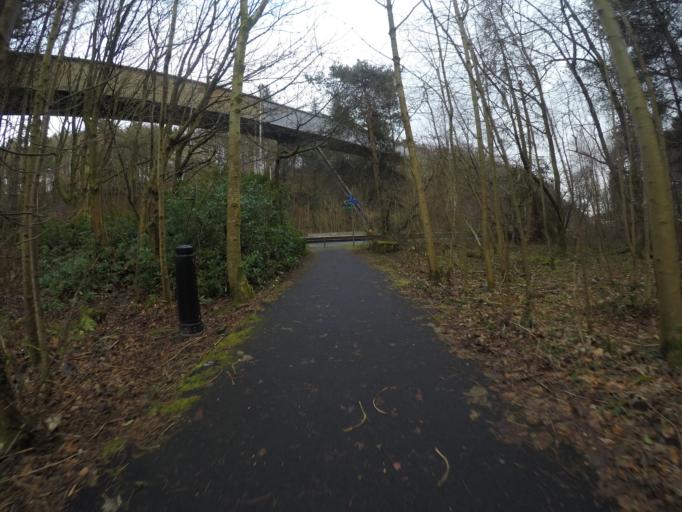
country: GB
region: Scotland
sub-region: North Ayrshire
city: Fairlie
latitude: 55.7289
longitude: -4.8662
